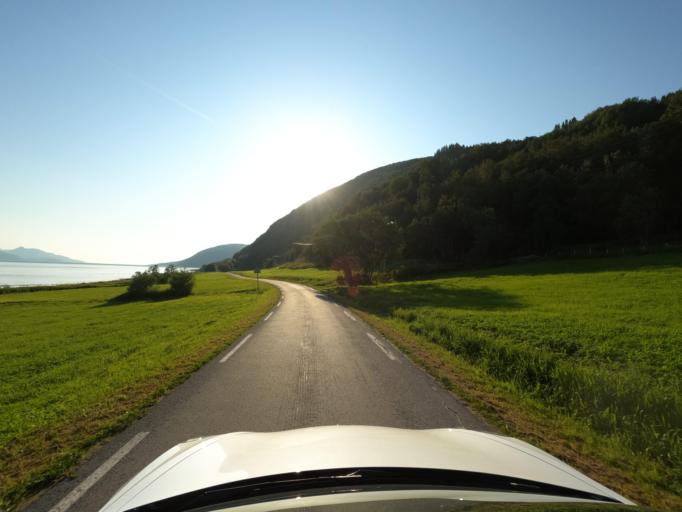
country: NO
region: Nordland
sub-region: Ballangen
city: Ballangen
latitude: 68.4690
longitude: 16.8548
